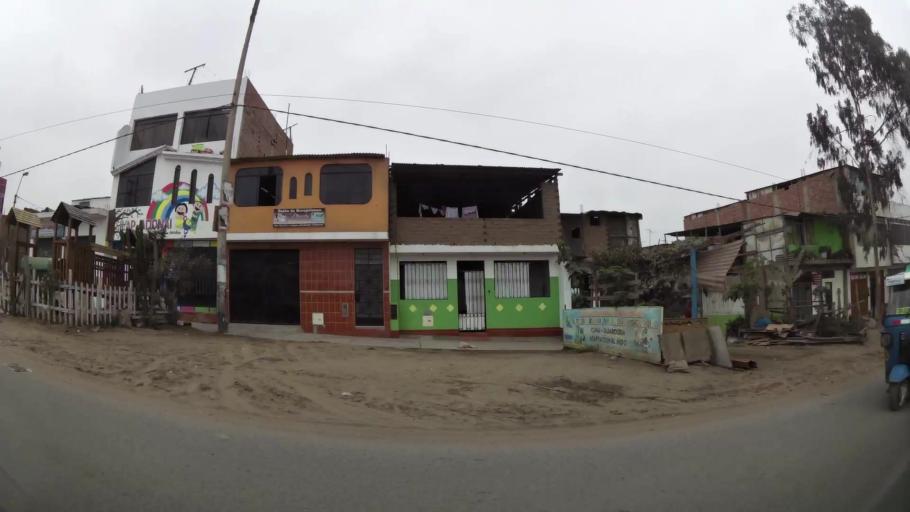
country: PE
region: Lima
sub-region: Lima
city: Surco
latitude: -12.2304
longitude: -76.9193
